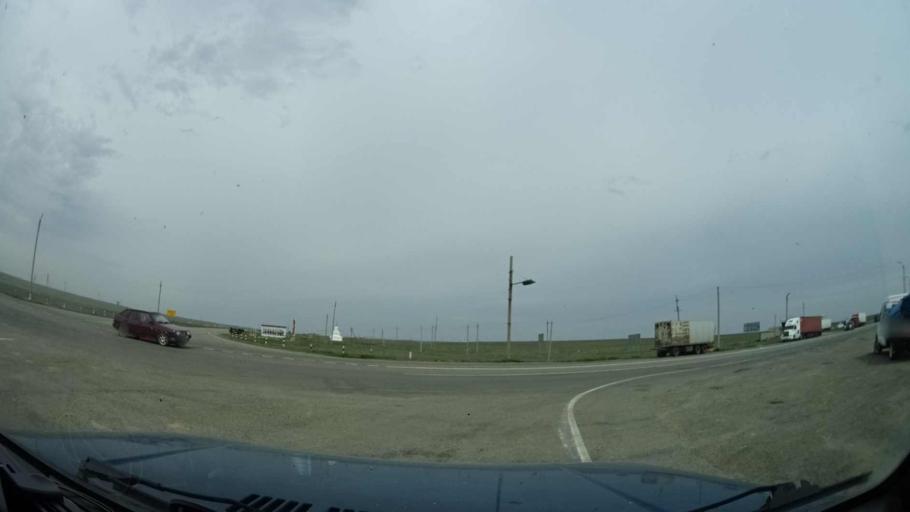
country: RU
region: Kalmykiya
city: Sovetskoye
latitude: 47.2988
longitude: 44.5734
